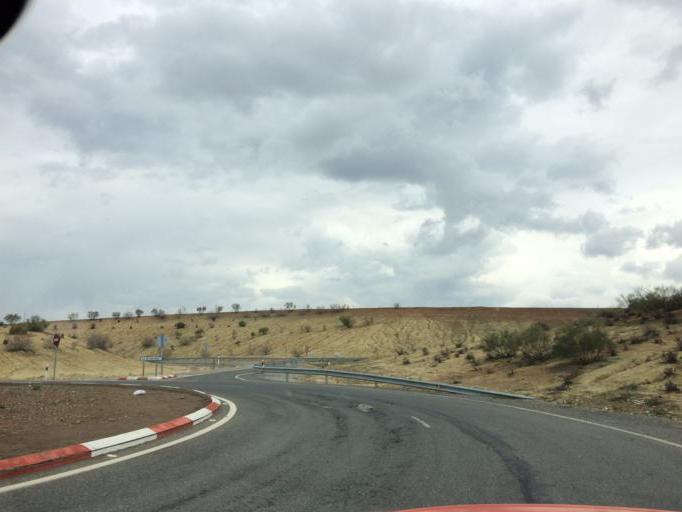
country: ES
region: Andalusia
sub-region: Provincia de Malaga
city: Antequera
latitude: 37.1119
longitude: -4.5631
